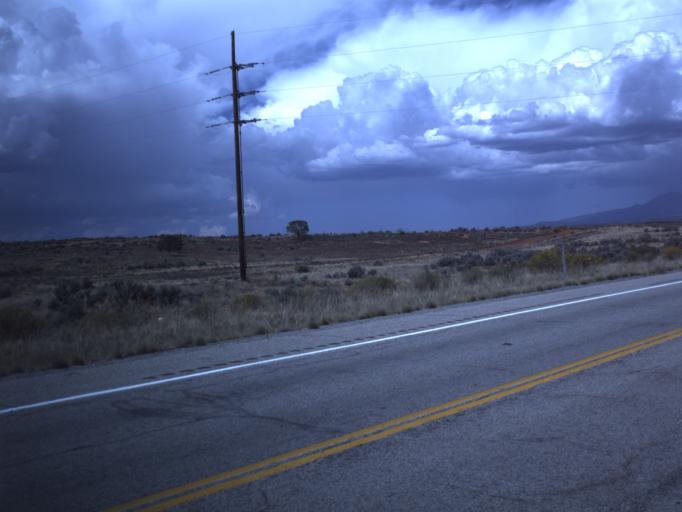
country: US
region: Utah
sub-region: San Juan County
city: Blanding
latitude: 37.5378
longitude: -109.4939
